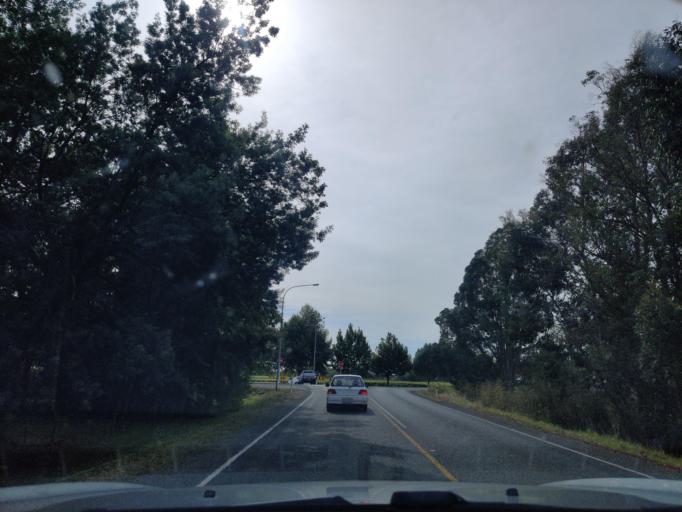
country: NZ
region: Marlborough
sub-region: Marlborough District
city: Blenheim
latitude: -41.5133
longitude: 173.8380
